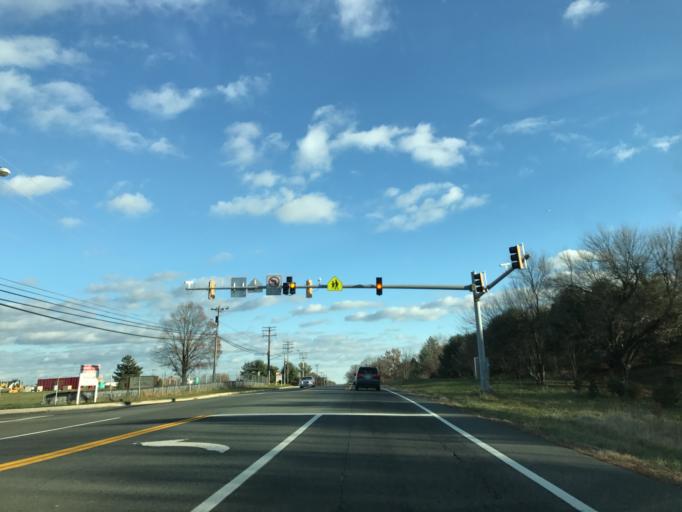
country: US
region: Maryland
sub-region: Harford County
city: Fallston
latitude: 39.5293
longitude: -76.4396
